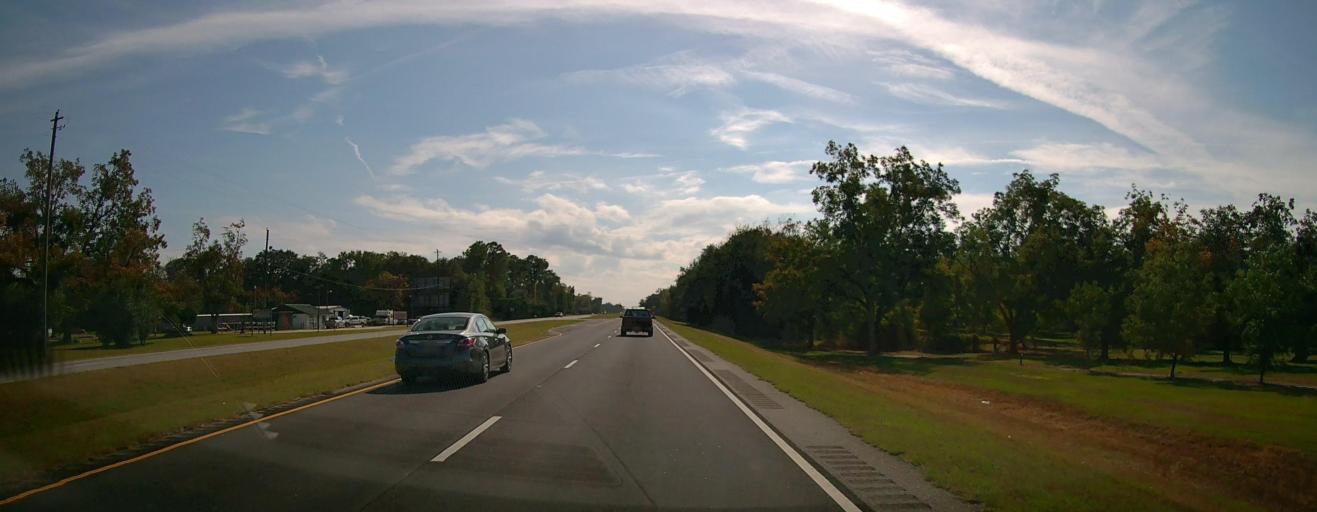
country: US
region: Georgia
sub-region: Dougherty County
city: Putney
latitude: 31.3860
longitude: -84.1485
